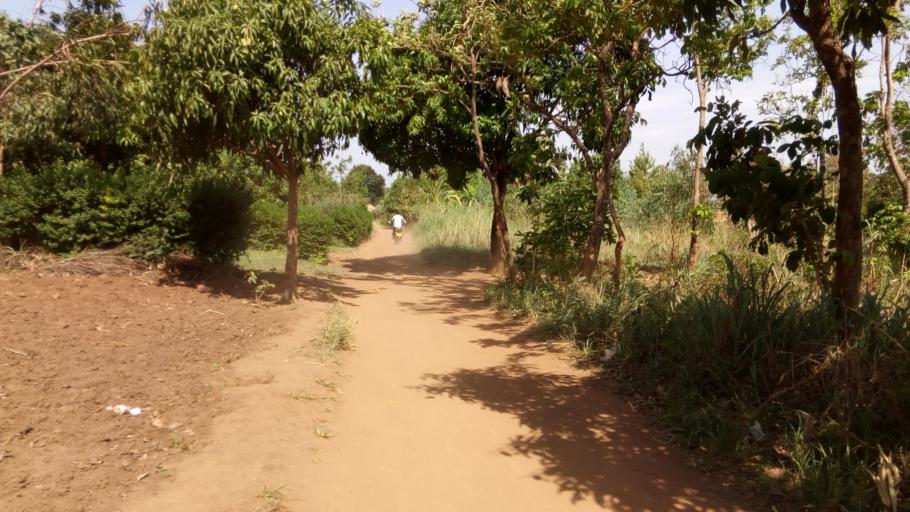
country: UG
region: Northern Region
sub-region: Gulu District
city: Gulu
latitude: 2.7964
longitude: 32.3186
